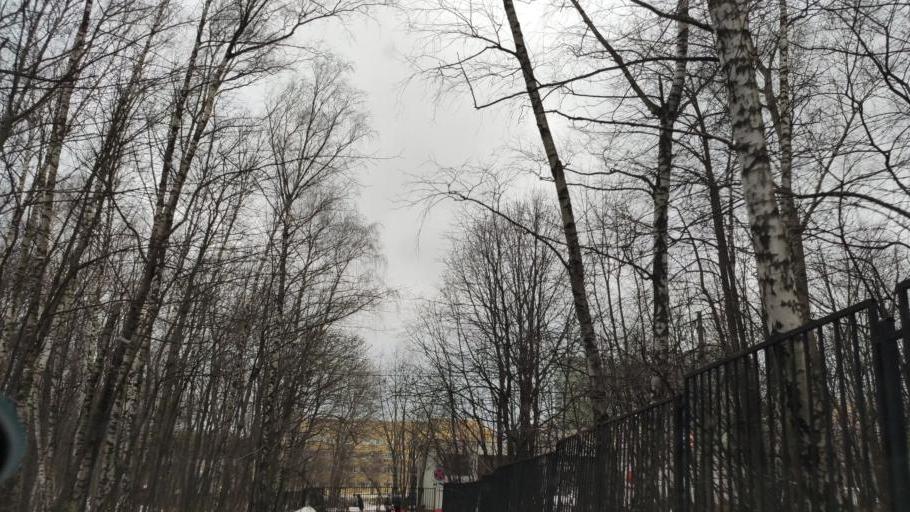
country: RU
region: Moscow
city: Yasenevo
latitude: 55.6135
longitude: 37.5290
